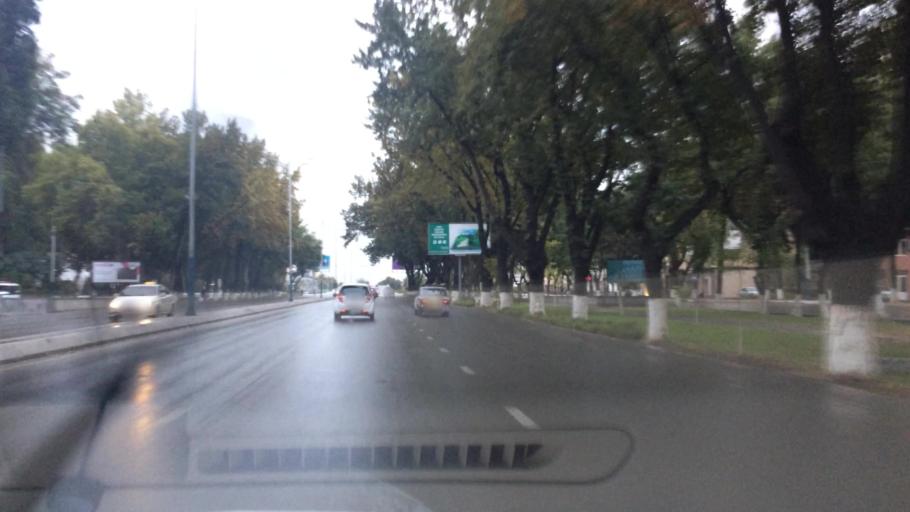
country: UZ
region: Toshkent Shahri
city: Tashkent
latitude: 41.2962
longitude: 69.2279
